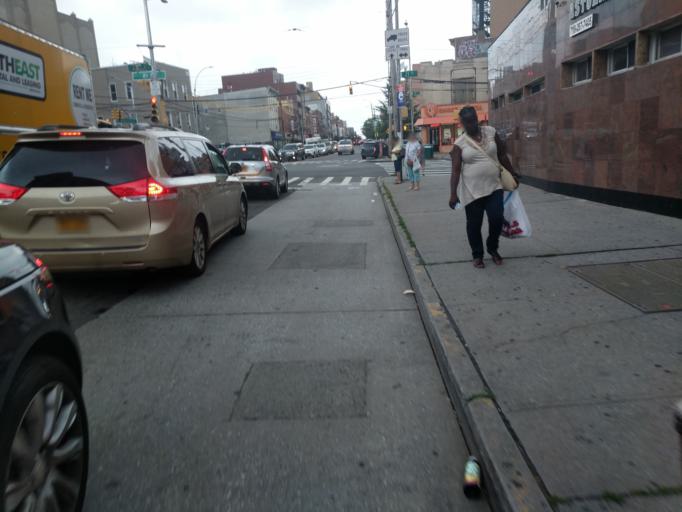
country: US
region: New York
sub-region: Queens County
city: Long Island City
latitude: 40.7723
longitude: -73.9264
